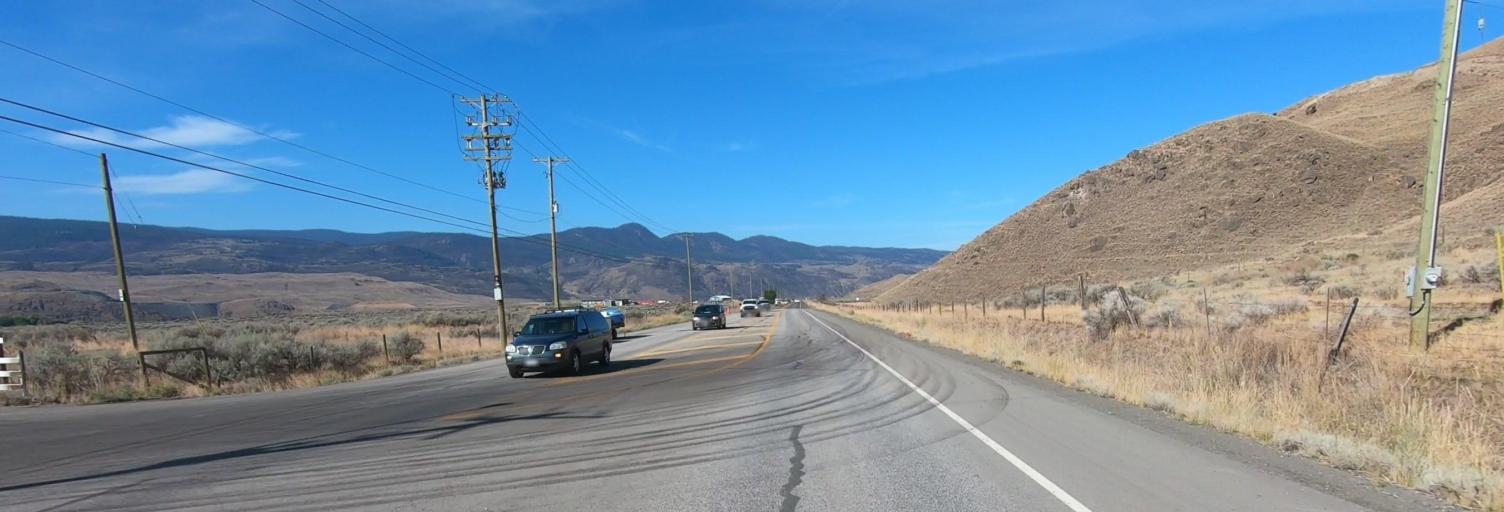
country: CA
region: British Columbia
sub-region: Thompson-Nicola Regional District
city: Ashcroft
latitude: 50.7671
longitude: -120.9699
